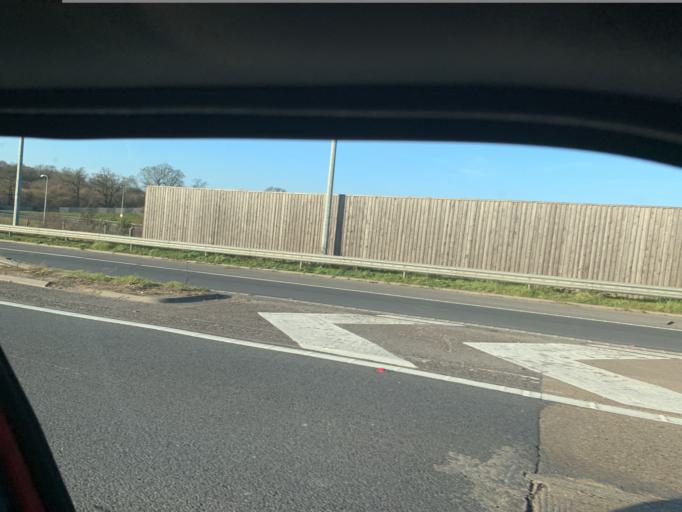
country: GB
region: England
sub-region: Surrey
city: Cobham
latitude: 51.3063
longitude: -0.4059
